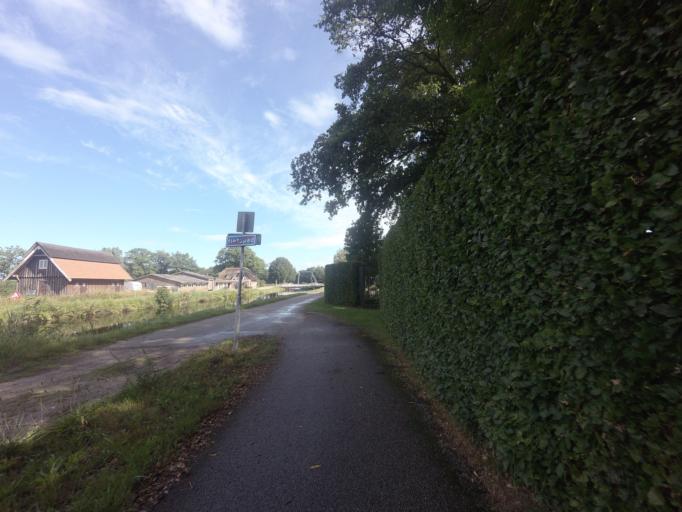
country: NL
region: Overijssel
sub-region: Gemeente Raalte
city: Raalte
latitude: 52.3366
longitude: 6.2693
